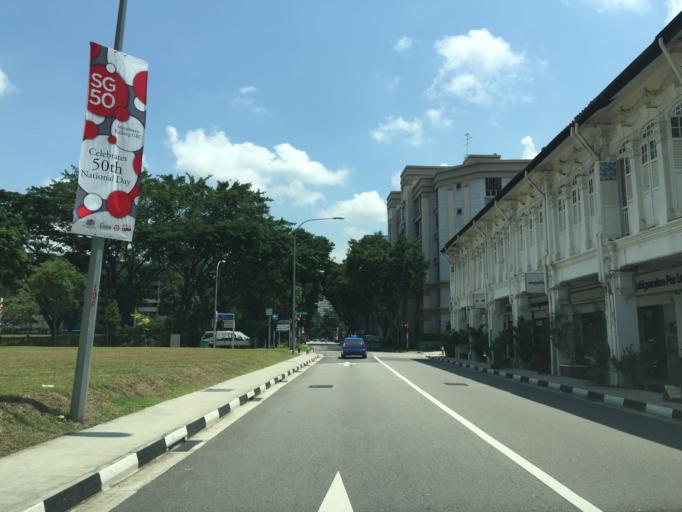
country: SG
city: Singapore
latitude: 1.3144
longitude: 103.8525
